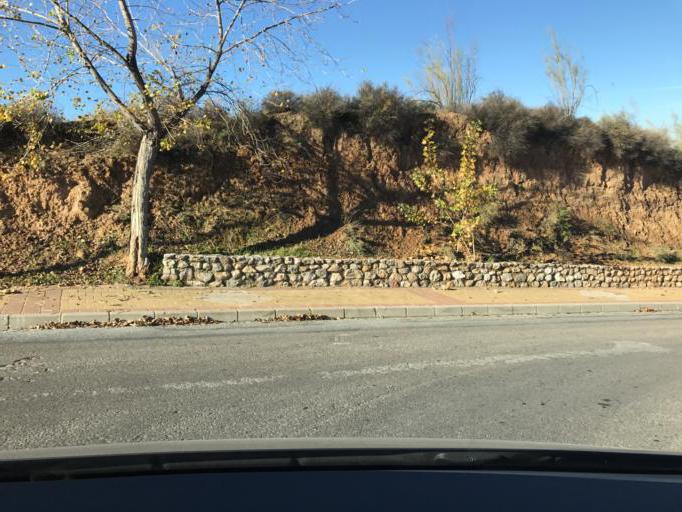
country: ES
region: Andalusia
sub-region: Provincia de Granada
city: Jun
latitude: 37.2101
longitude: -3.5900
